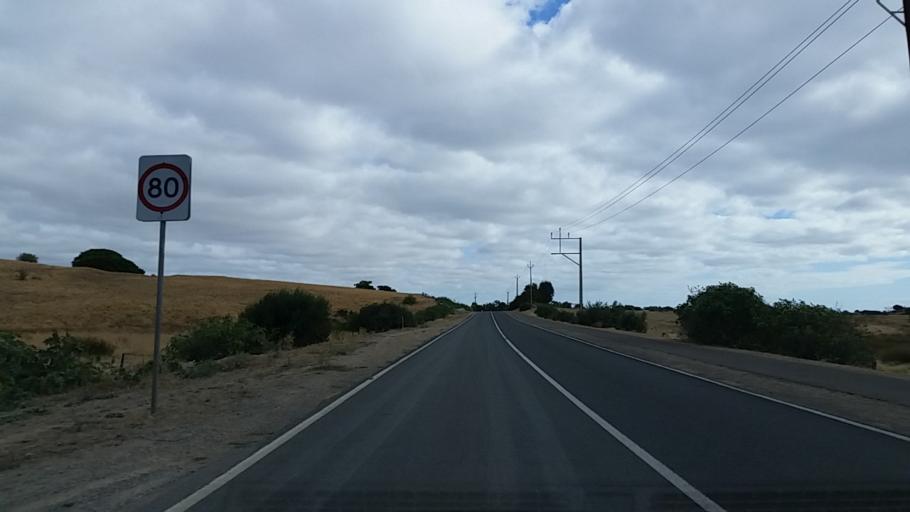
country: AU
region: South Australia
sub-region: Yankalilla
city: Normanville
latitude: -35.4323
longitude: 138.3243
